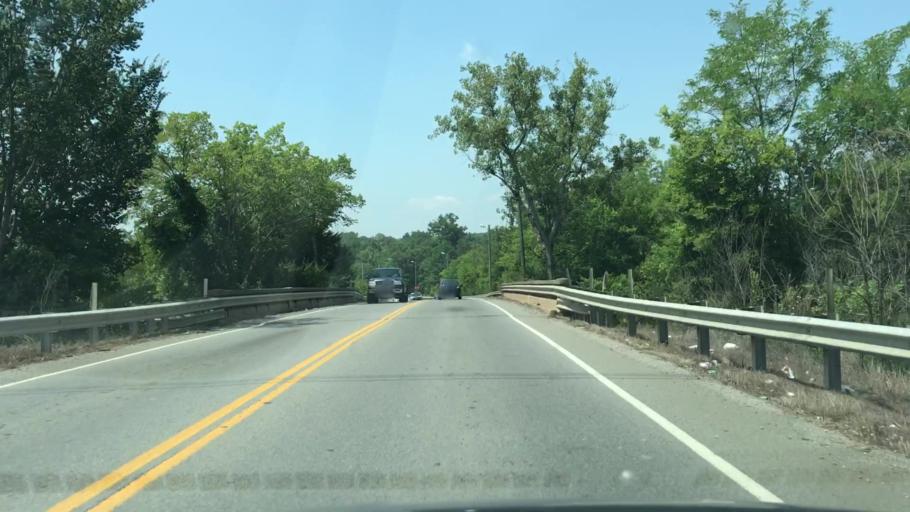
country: US
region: Tennessee
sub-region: Rutherford County
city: La Vergne
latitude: 36.0287
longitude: -86.6139
